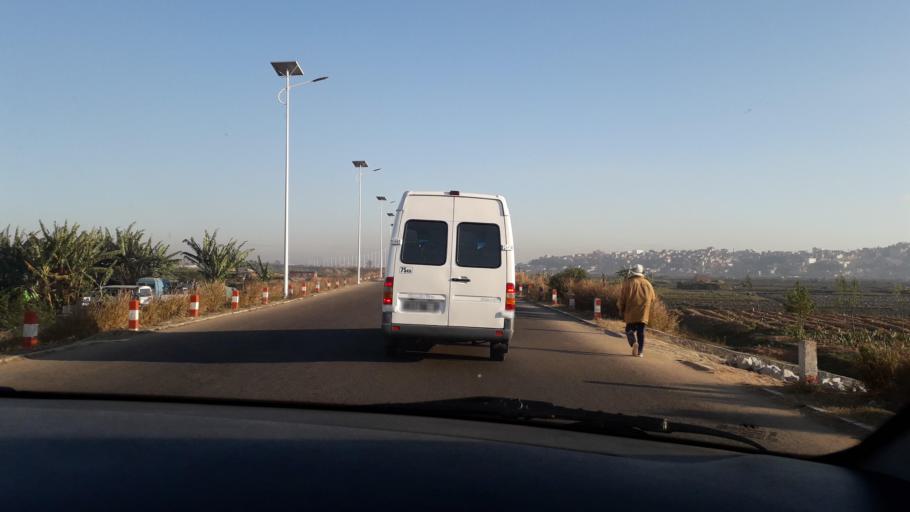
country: MG
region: Analamanga
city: Antananarivo
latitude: -18.8859
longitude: 47.4920
